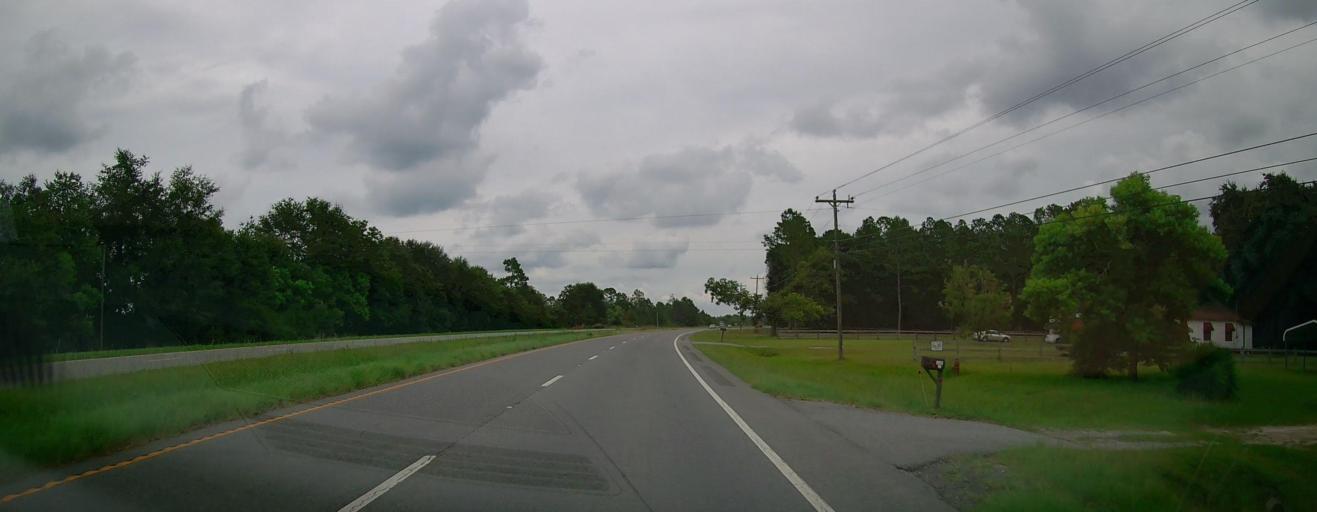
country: US
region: Georgia
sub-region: Appling County
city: Baxley
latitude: 31.8222
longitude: -82.4696
